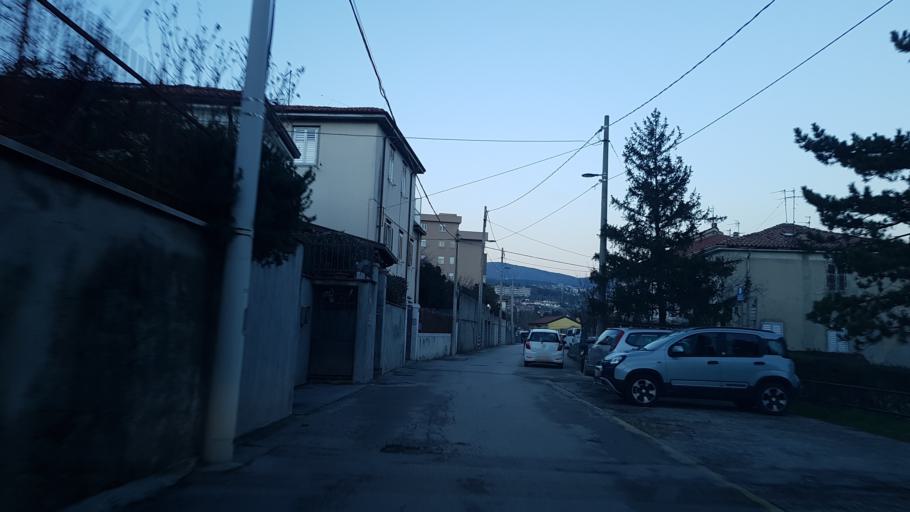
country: IT
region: Friuli Venezia Giulia
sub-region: Provincia di Trieste
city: Trieste
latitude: 45.6273
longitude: 13.7917
